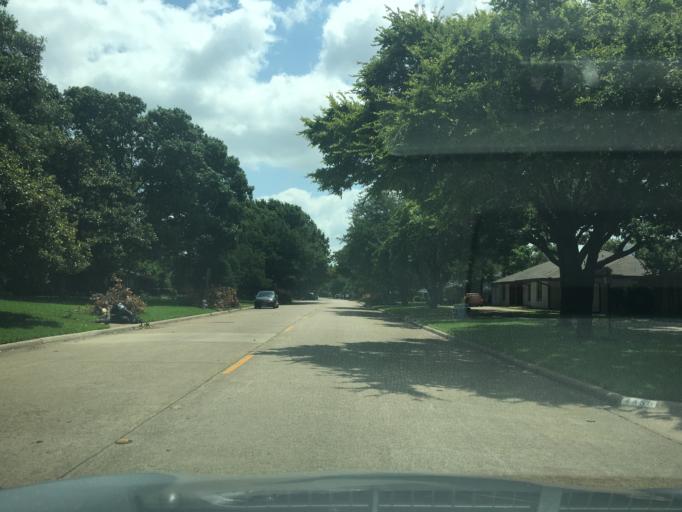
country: US
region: Texas
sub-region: Dallas County
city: Addison
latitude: 32.9224
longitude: -96.8325
